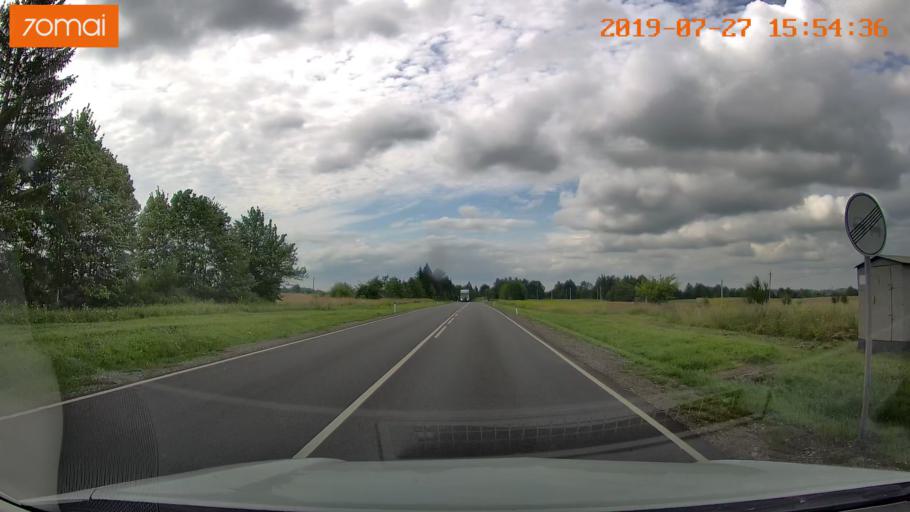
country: RU
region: Kaliningrad
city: Chernyakhovsk
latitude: 54.6084
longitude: 21.9367
